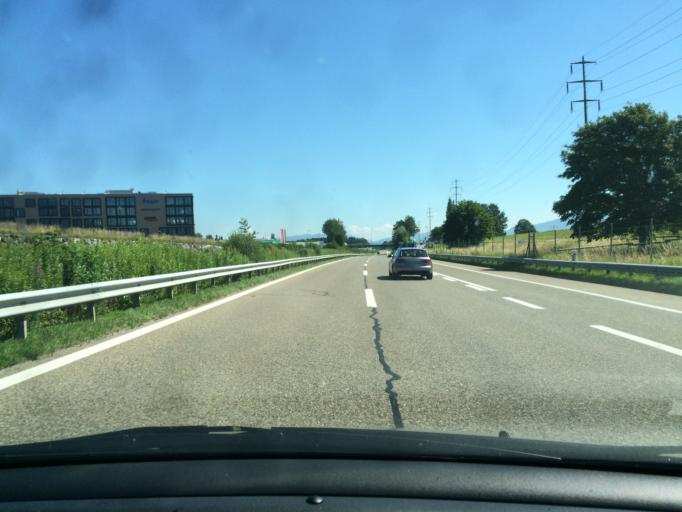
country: AT
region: Vorarlberg
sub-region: Politischer Bezirk Feldkirch
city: Mader
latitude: 47.3568
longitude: 9.6065
